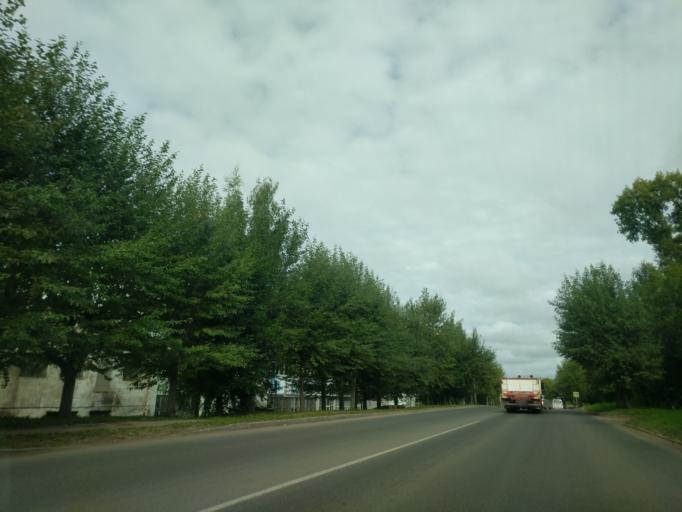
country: RU
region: Kirov
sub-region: Kirovo-Chepetskiy Rayon
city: Kirov
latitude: 58.6015
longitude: 49.6446
